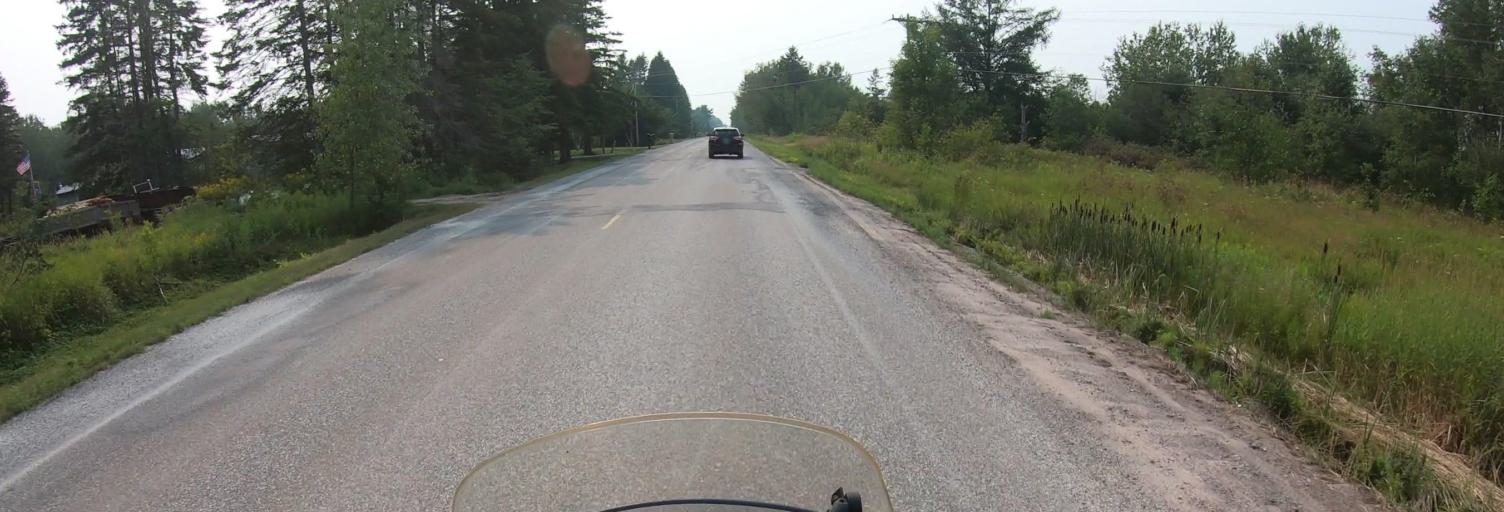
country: US
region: Michigan
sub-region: Chippewa County
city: Sault Ste. Marie
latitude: 46.4627
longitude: -84.3020
